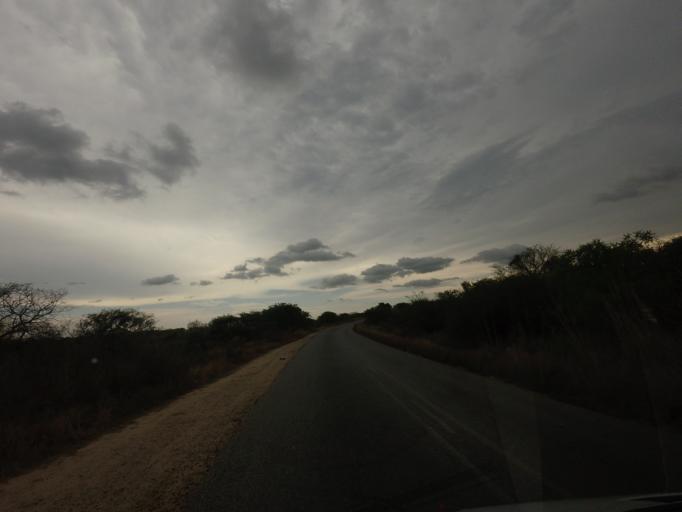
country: ZA
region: Limpopo
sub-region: Mopani District Municipality
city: Hoedspruit
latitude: -24.5301
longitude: 30.9938
